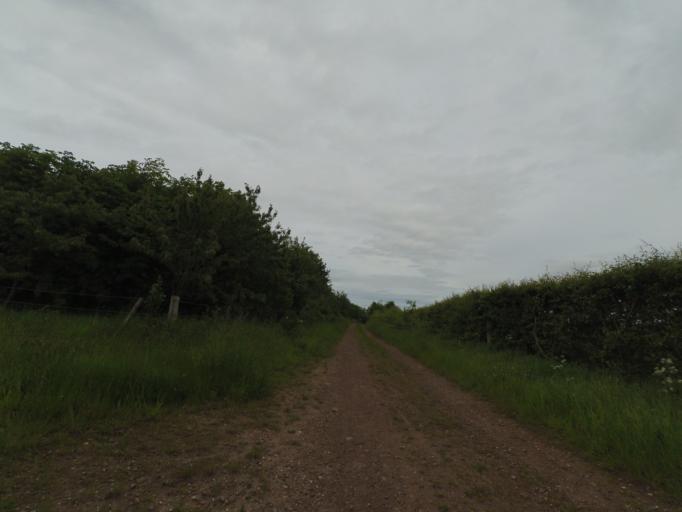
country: GB
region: Scotland
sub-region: East Lothian
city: Macmerry
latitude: 55.9476
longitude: -2.9246
